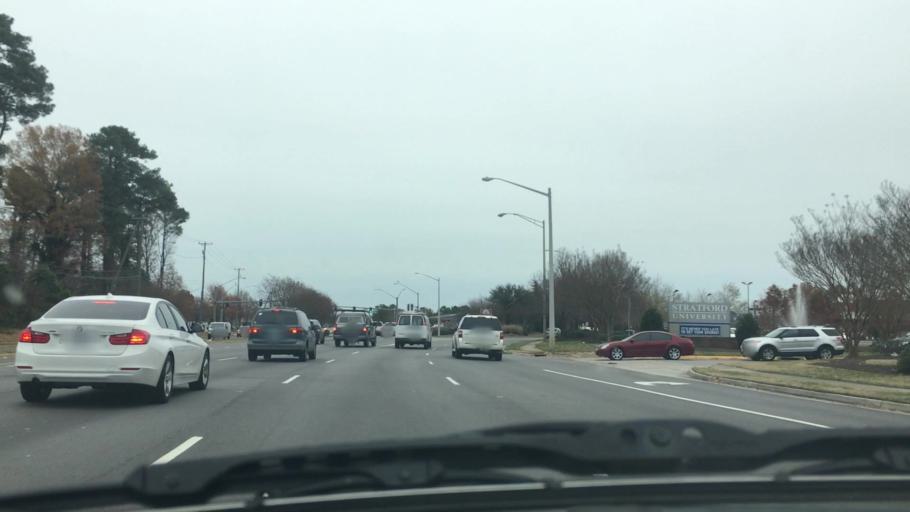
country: US
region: Virginia
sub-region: City of Chesapeake
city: Chesapeake
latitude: 36.8244
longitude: -76.1283
